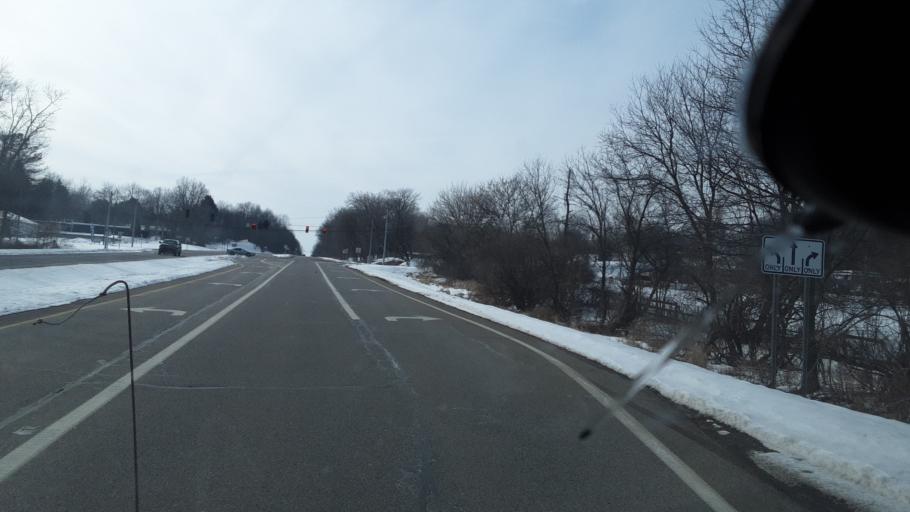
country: US
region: Ohio
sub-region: Summit County
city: Mogadore
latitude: 41.0274
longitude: -81.3455
